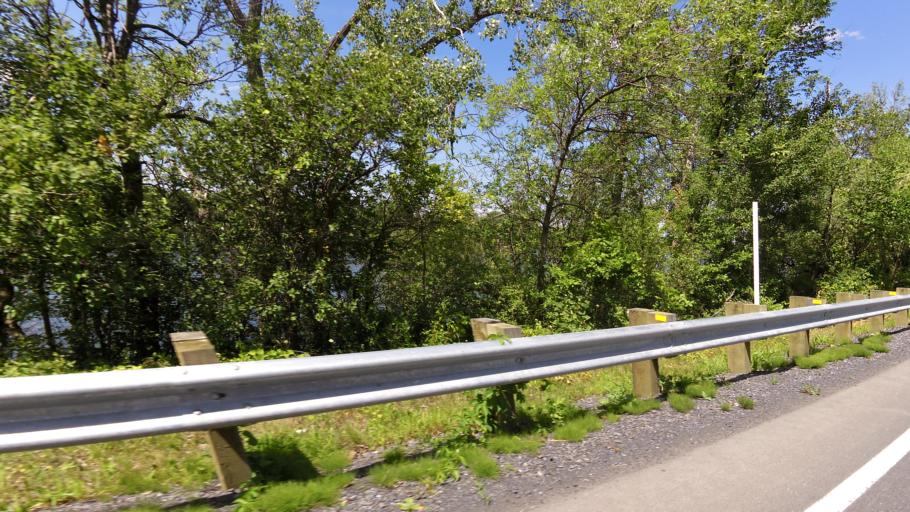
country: CA
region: Quebec
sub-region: Monteregie
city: Richelieu
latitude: 45.3755
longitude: -73.2455
